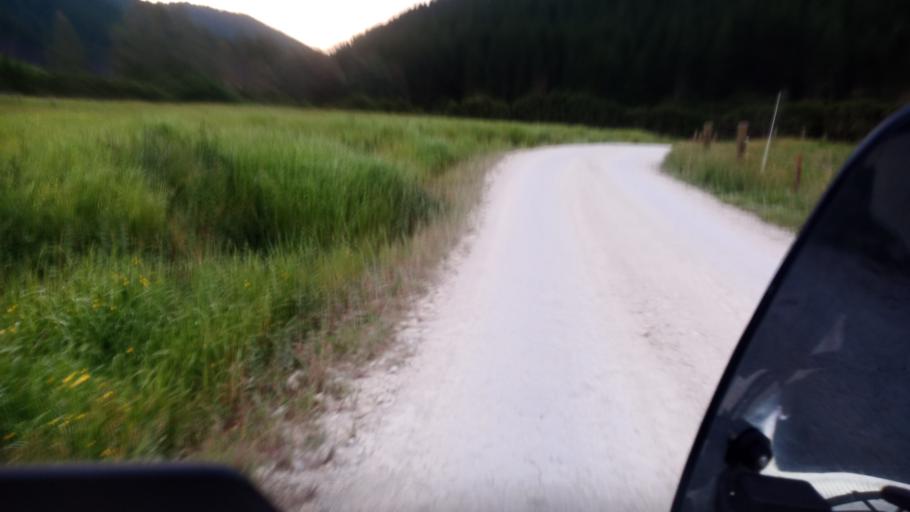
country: NZ
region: Gisborne
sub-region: Gisborne District
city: Gisborne
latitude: -38.4646
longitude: 177.9670
